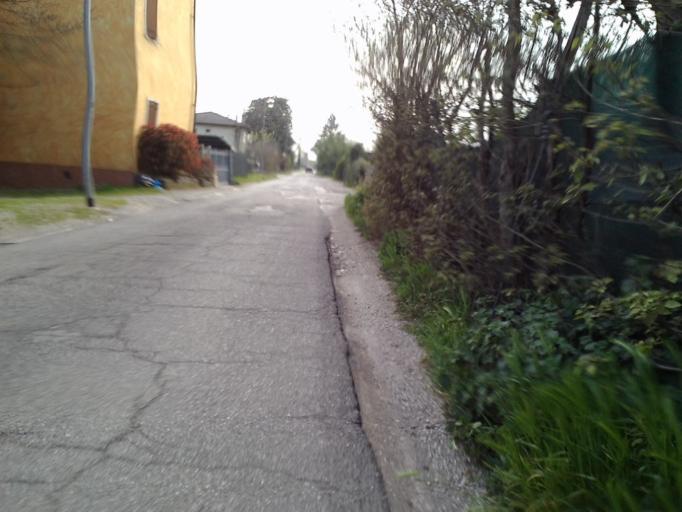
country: IT
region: Veneto
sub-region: Provincia di Verona
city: Beccacivetta-Azzano
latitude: 45.4056
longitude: 10.9463
